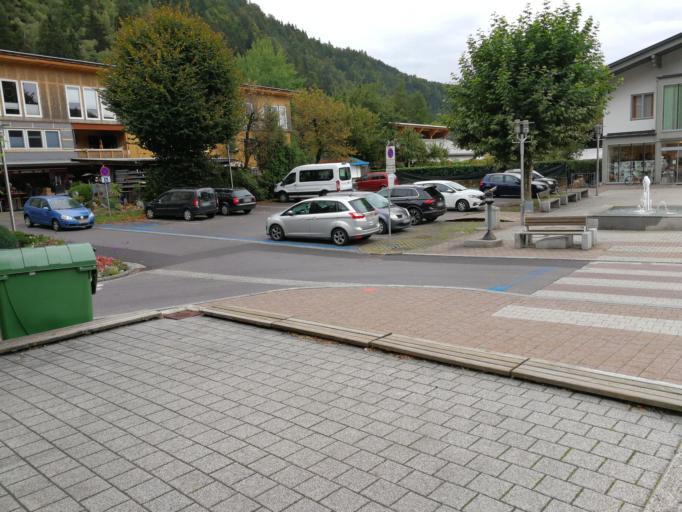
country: AT
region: Carinthia
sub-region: Politischer Bezirk Villach Land
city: Ferndorf
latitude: 46.7822
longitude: 13.6583
